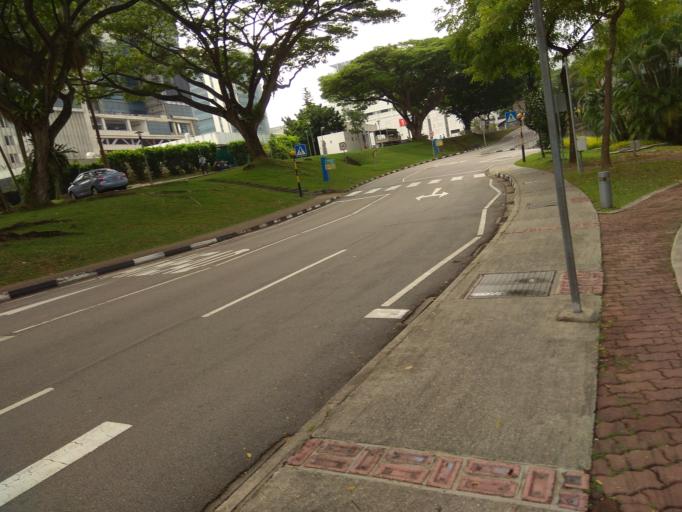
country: SG
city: Singapore
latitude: 1.2969
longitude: 103.7821
